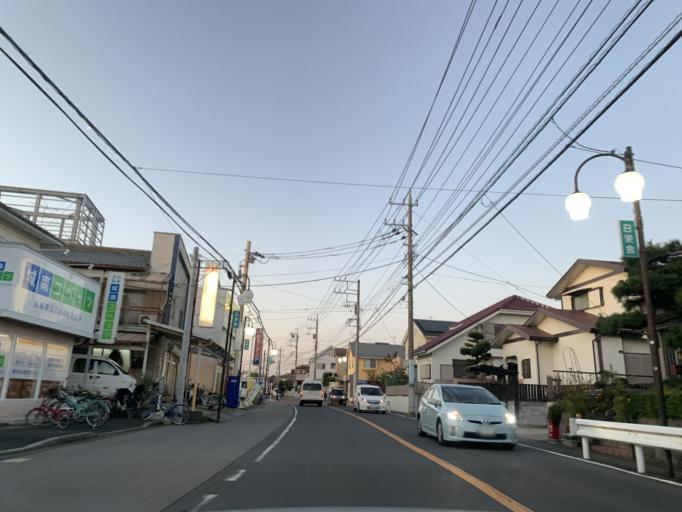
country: JP
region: Chiba
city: Nagareyama
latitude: 35.9000
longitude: 139.9072
